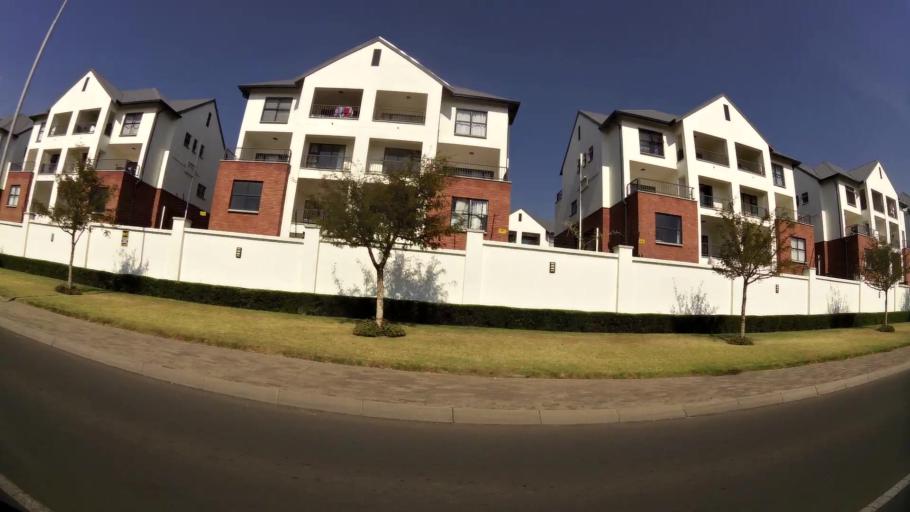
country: ZA
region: Gauteng
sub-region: City of Johannesburg Metropolitan Municipality
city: Modderfontein
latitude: -26.1172
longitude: 28.1615
